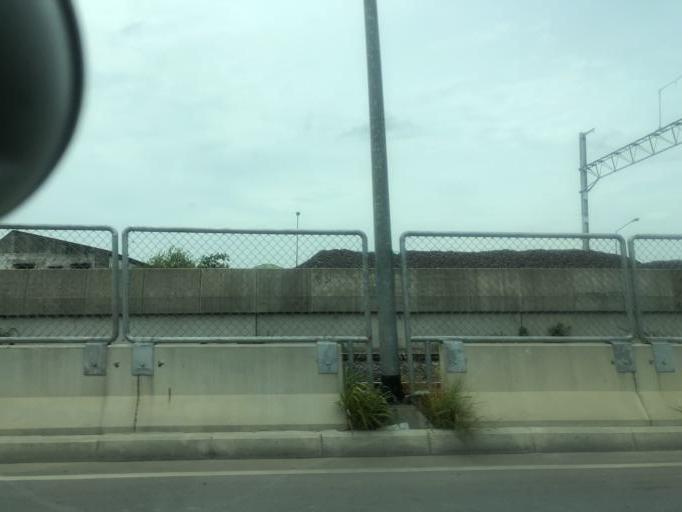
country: TH
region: Bangkok
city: Don Mueang
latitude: 13.9450
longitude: 100.6076
